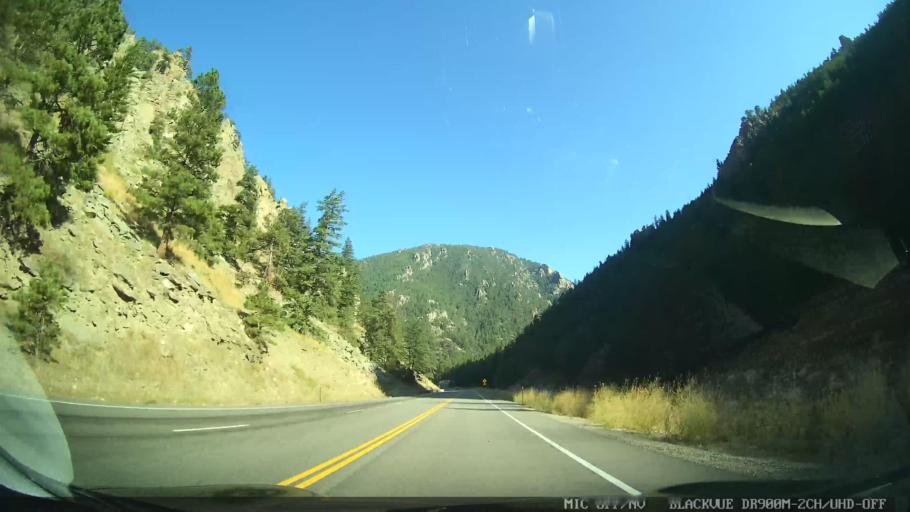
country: US
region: Colorado
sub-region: Larimer County
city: Estes Park
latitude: 40.4152
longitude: -105.3702
